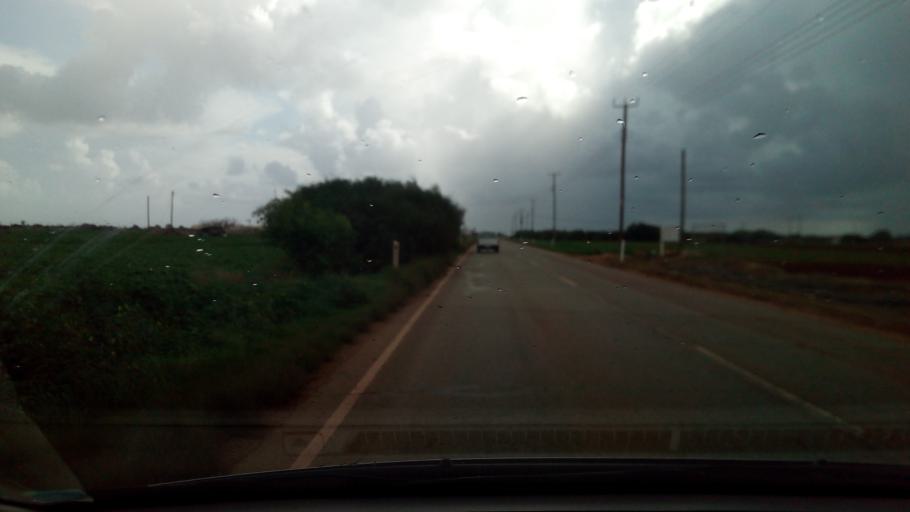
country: CY
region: Ammochostos
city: Liopetri
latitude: 34.9888
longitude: 33.8932
